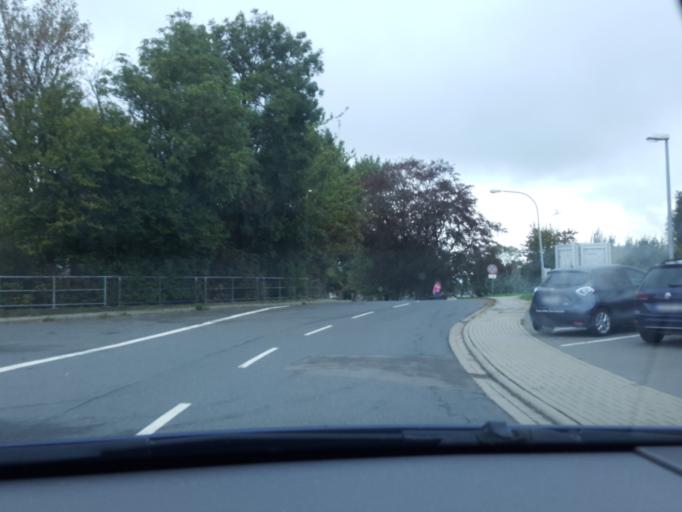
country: DE
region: Lower Saxony
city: Emden
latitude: 53.3371
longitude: 7.1867
